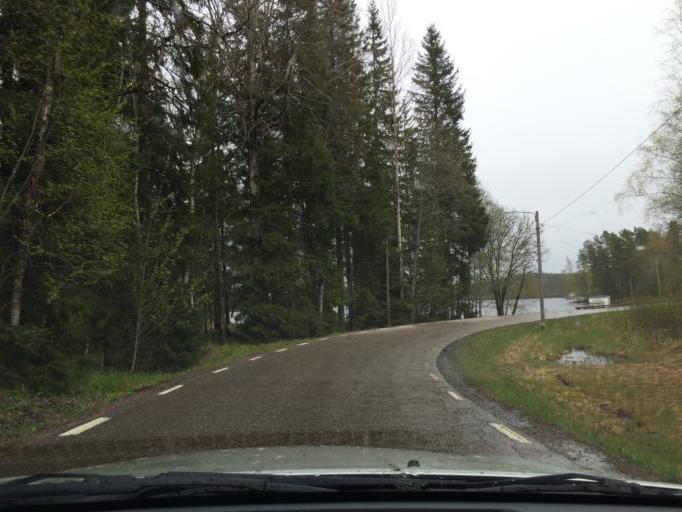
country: SE
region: Dalarna
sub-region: Ludvika Kommun
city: Abborrberget
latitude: 60.0464
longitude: 14.7717
